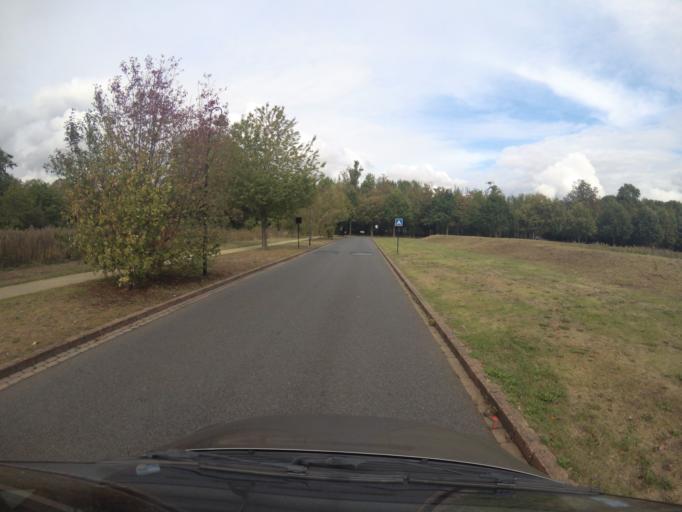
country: FR
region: Ile-de-France
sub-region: Departement de Seine-et-Marne
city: Chessy
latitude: 48.8743
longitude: 2.7671
